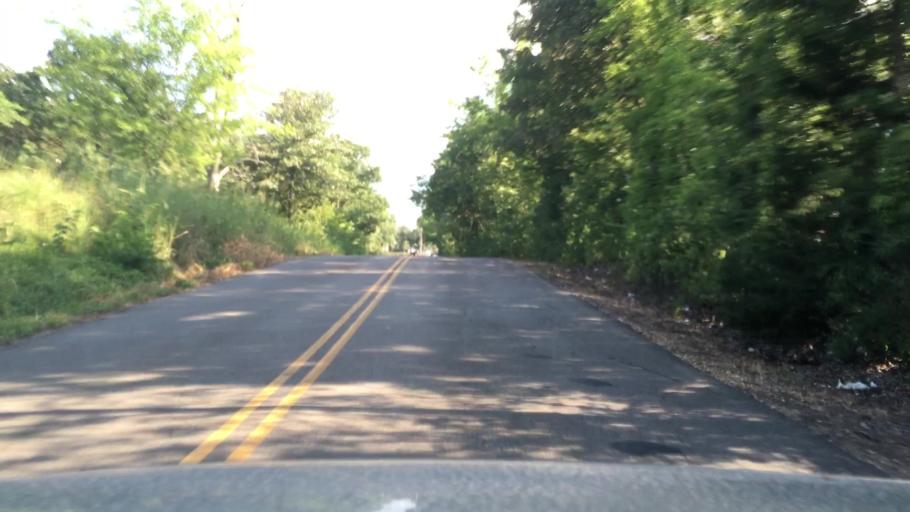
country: US
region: Oklahoma
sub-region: Muskogee County
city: Fort Gibson
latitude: 35.9118
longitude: -95.1587
